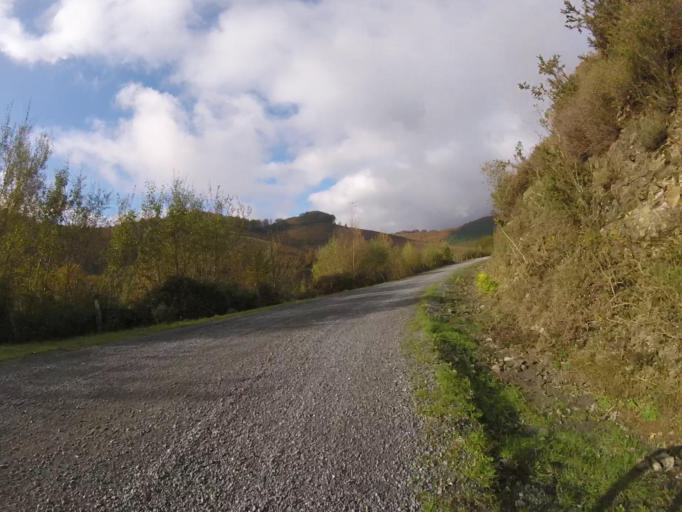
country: ES
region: Navarre
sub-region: Provincia de Navarra
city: Goizueta
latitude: 43.2086
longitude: -1.8308
